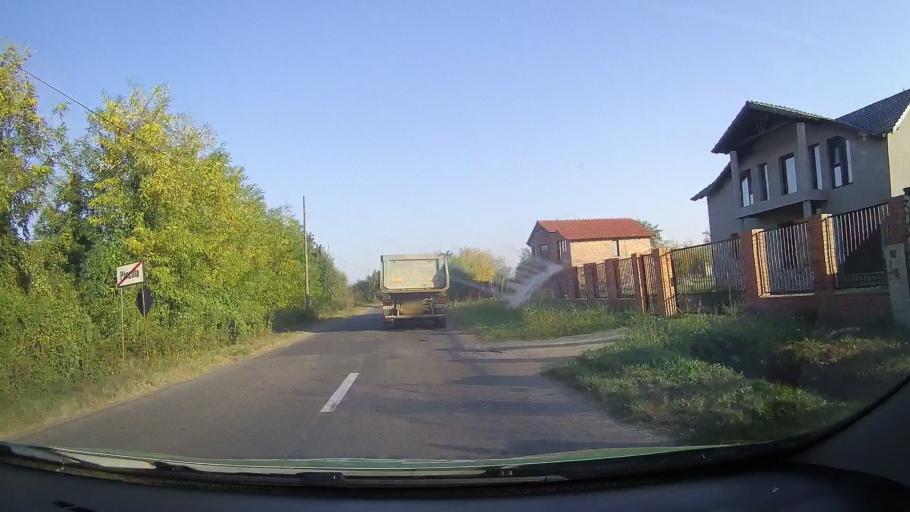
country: RO
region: Arad
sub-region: Comuna Pancota
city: Pancota
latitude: 46.3167
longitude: 21.6992
